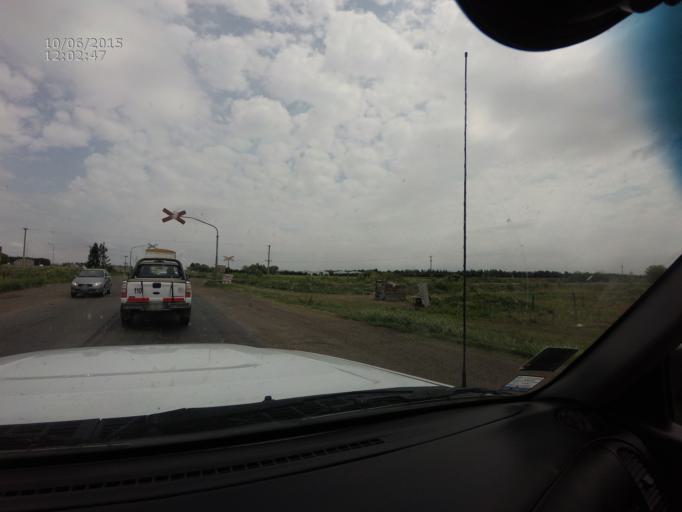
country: AR
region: Santa Fe
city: Perez
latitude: -33.0921
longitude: -60.7833
